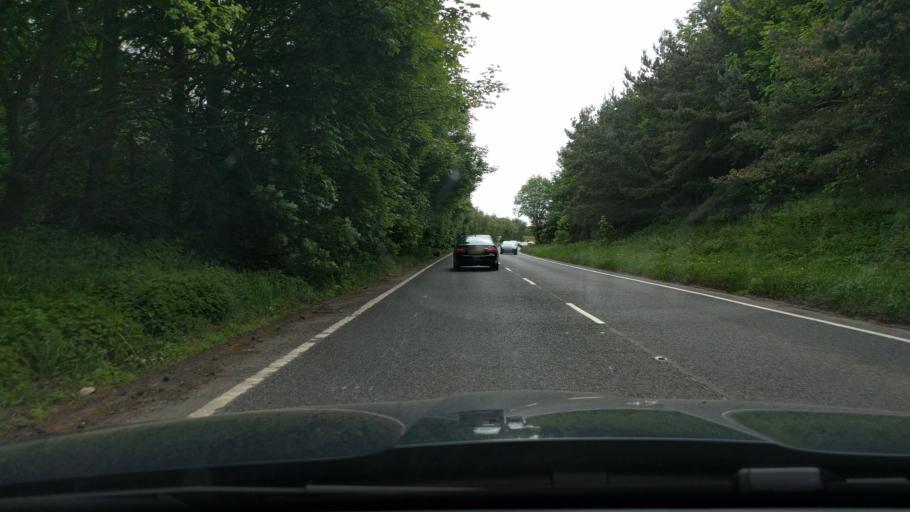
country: GB
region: England
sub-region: Northumberland
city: Lynemouth
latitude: 55.1941
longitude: -1.5431
